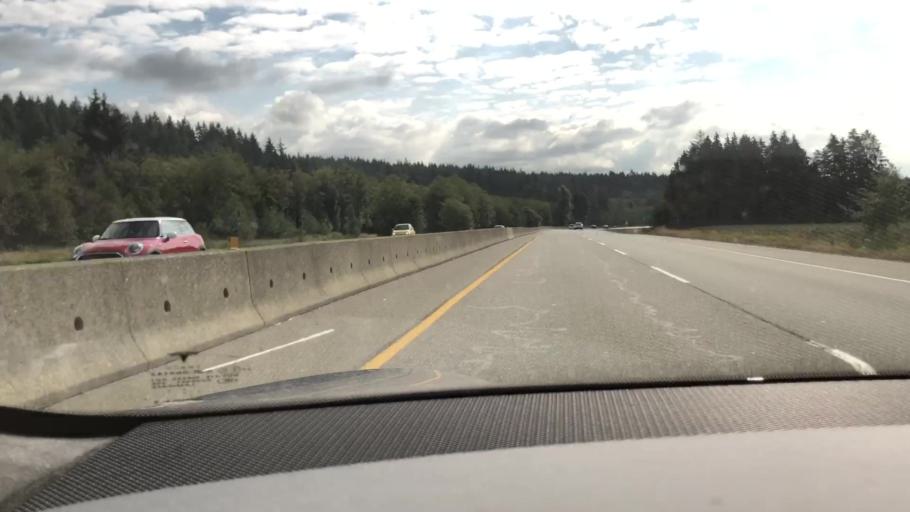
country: CA
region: British Columbia
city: Delta
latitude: 49.1145
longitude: -122.9166
